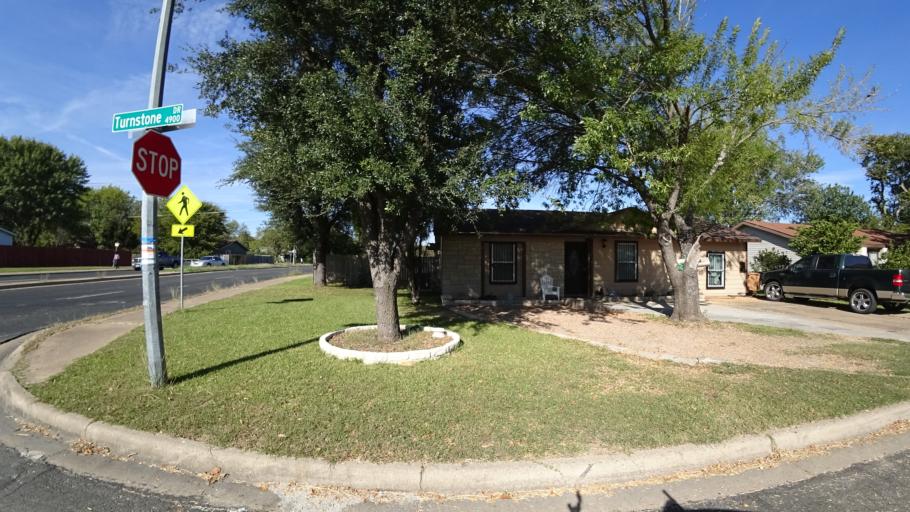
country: US
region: Texas
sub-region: Travis County
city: Onion Creek
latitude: 30.1870
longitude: -97.7461
